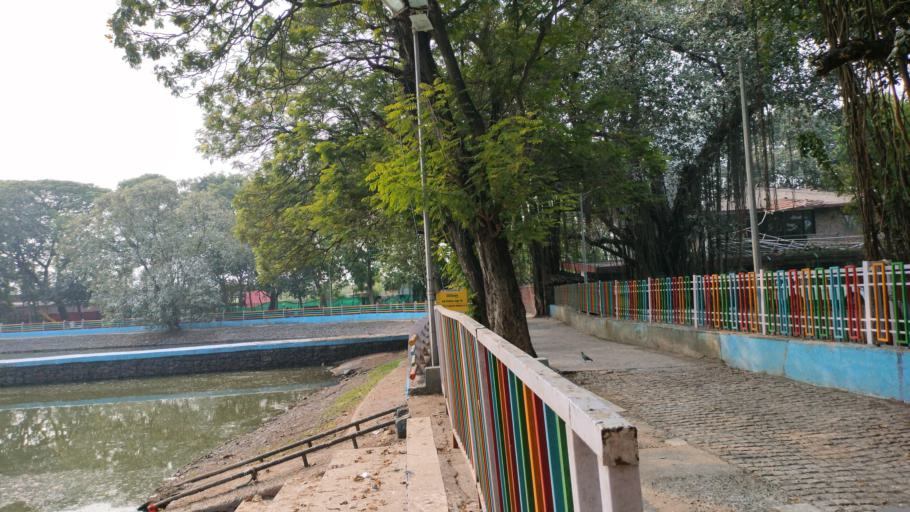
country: IN
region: Maharashtra
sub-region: Thane
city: Navi Mumbai
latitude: 19.0718
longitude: 72.9850
